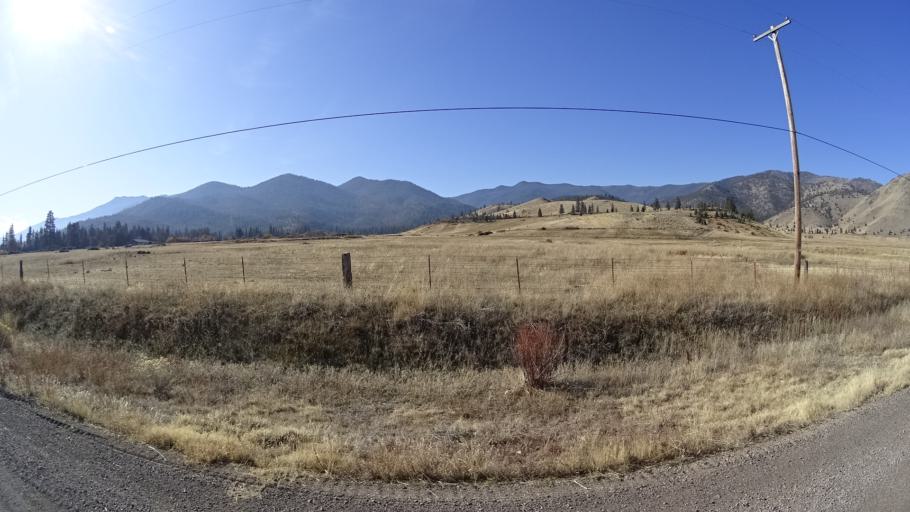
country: US
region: California
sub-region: Siskiyou County
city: Weed
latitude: 41.4511
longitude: -122.4547
